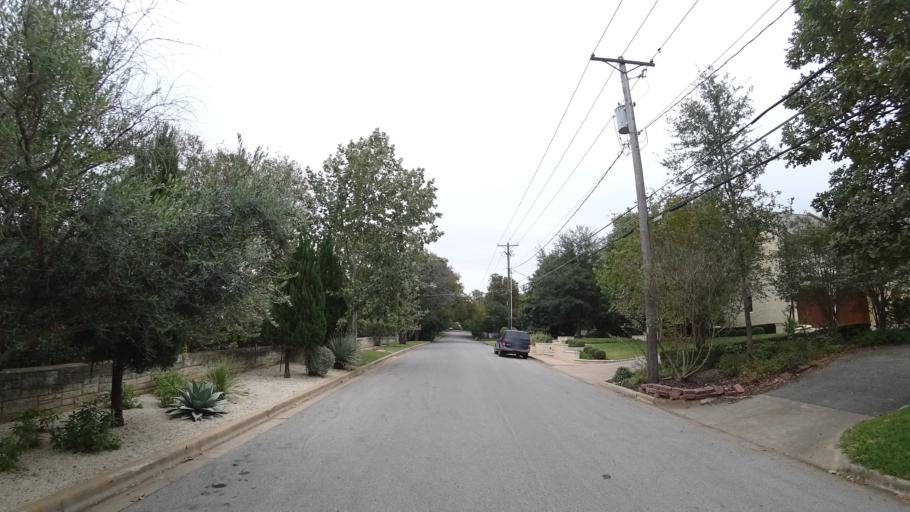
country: US
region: Texas
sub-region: Travis County
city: West Lake Hills
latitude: 30.3001
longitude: -97.7722
